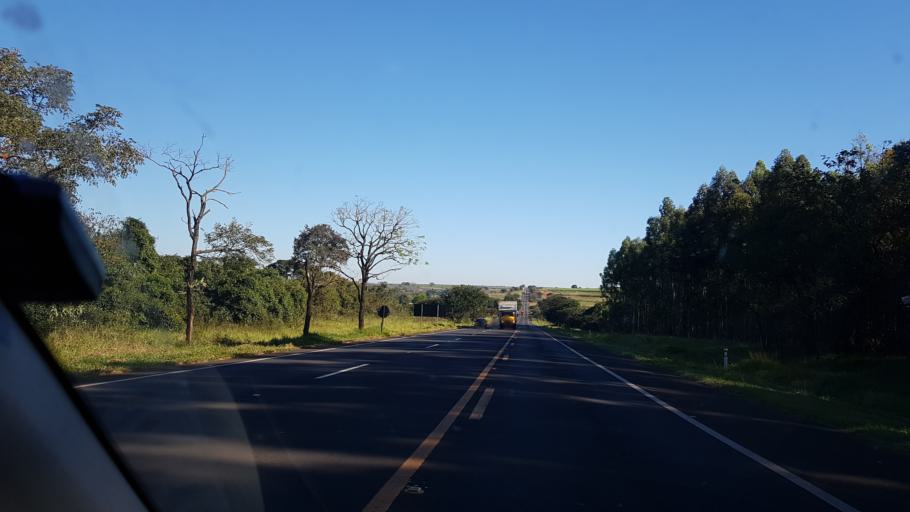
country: BR
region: Sao Paulo
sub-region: Assis
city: Assis
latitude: -22.6148
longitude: -50.4614
